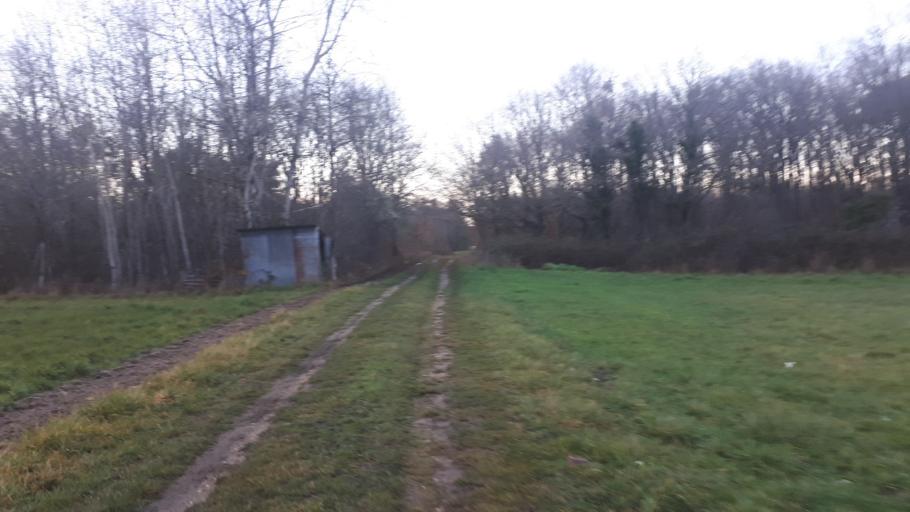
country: FR
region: Centre
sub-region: Departement du Loir-et-Cher
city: Saint-Romain-sur-Cher
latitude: 47.3469
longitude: 1.4006
